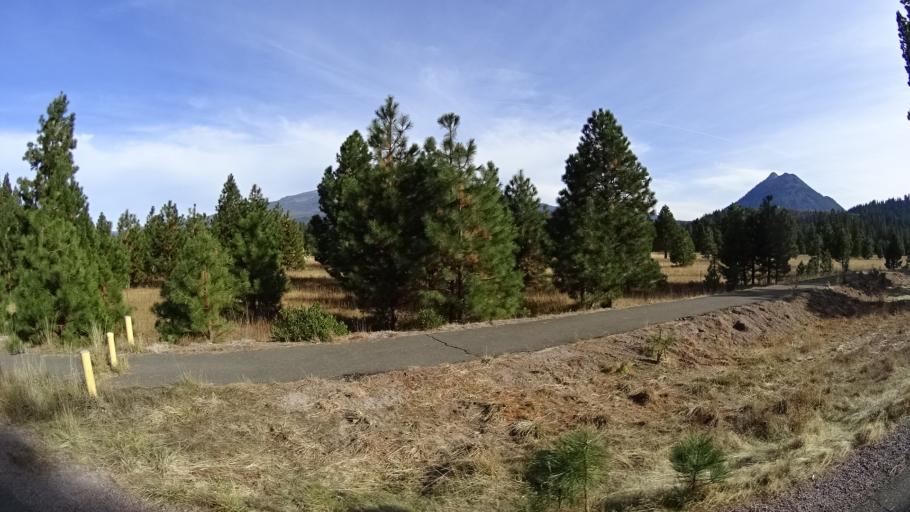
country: US
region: California
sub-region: Siskiyou County
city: Weed
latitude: 41.3989
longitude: -122.3893
